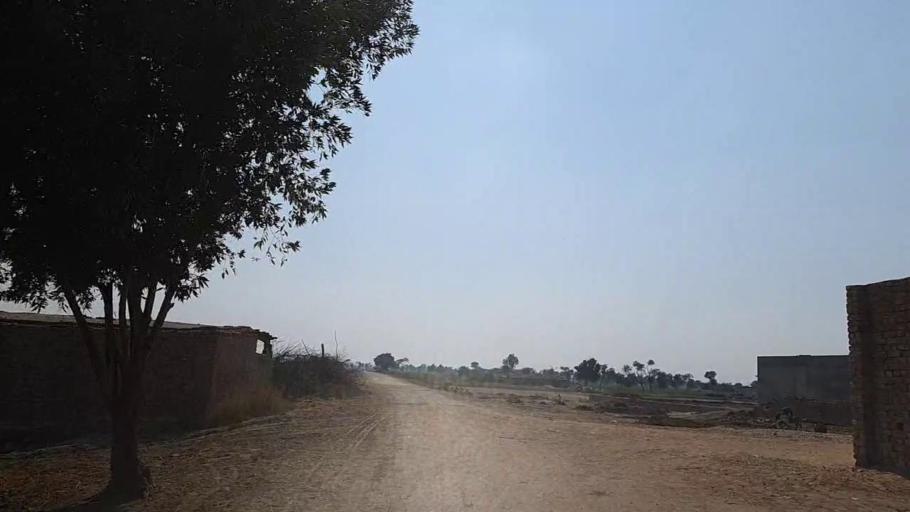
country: PK
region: Sindh
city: Daur
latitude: 26.4565
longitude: 68.2709
